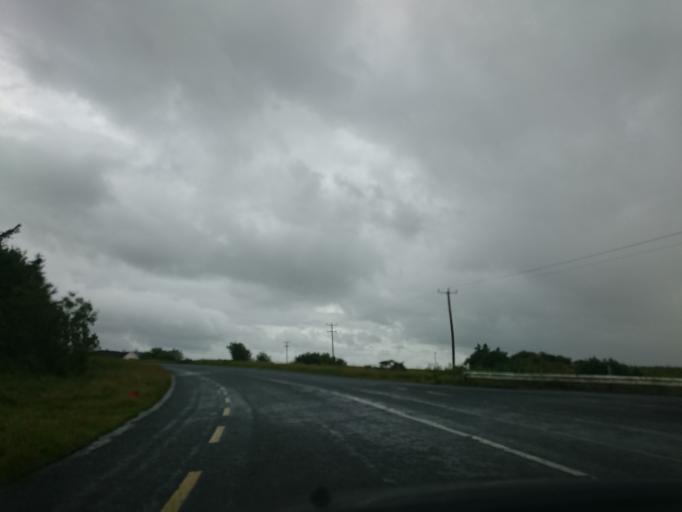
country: IE
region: Connaught
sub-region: Maigh Eo
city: Ballina
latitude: 54.1937
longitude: -9.2034
